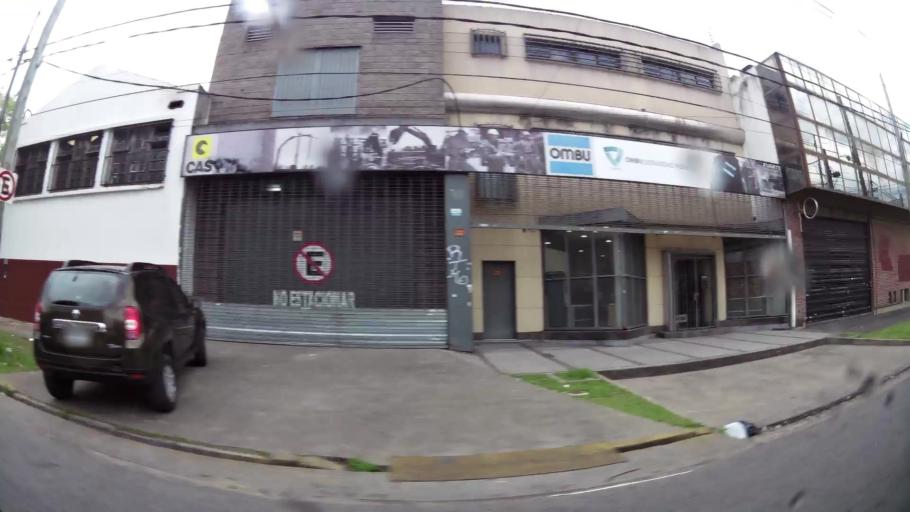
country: AR
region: Buenos Aires
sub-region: Partido de Lanus
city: Lanus
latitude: -34.6920
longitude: -58.3995
